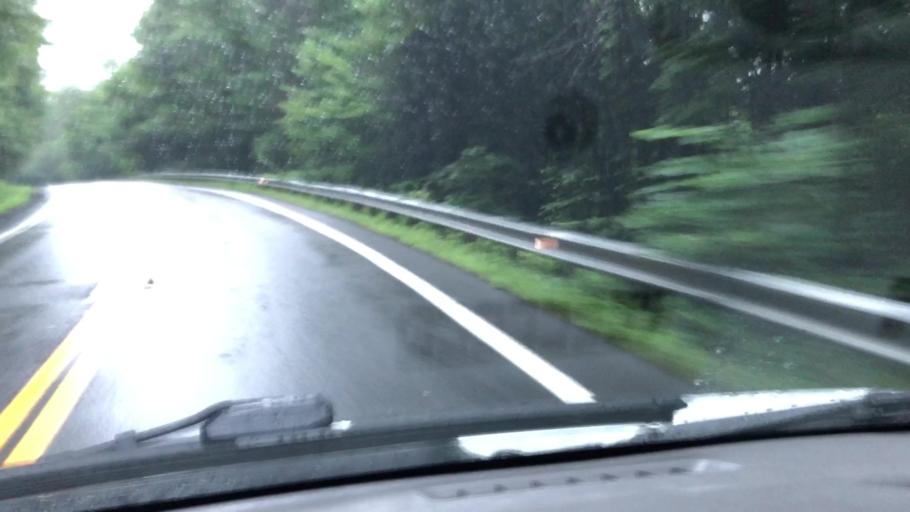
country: US
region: Massachusetts
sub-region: Hampshire County
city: Westhampton
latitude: 42.3064
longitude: -72.8611
